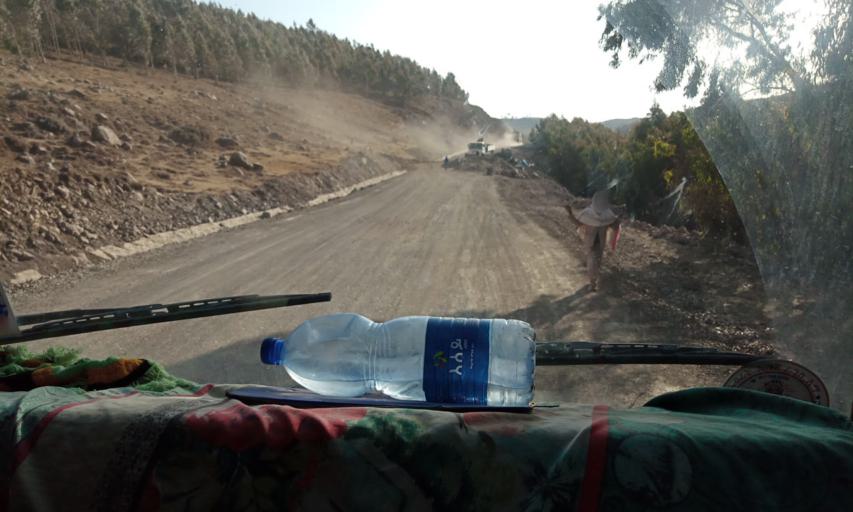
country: ET
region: Amhara
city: Debre Sina
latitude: 9.6751
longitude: 39.7256
